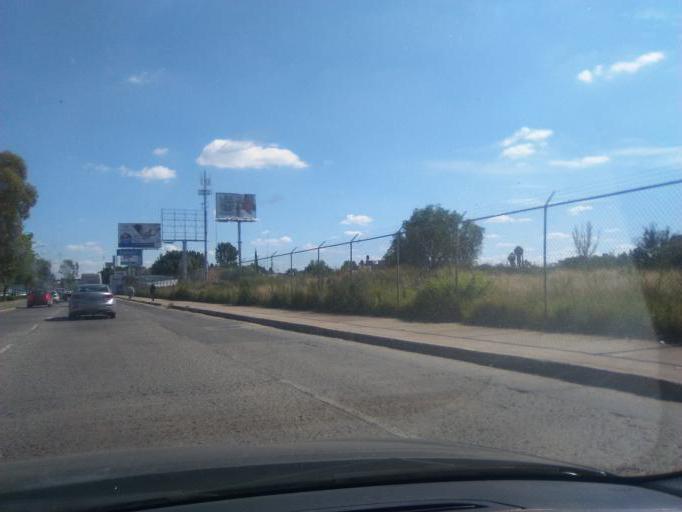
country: MX
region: Guanajuato
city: Leon
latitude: 21.1122
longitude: -101.6490
